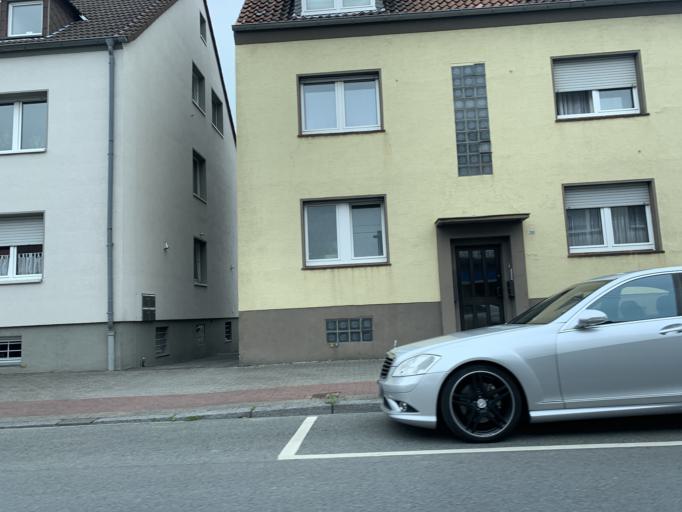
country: DE
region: North Rhine-Westphalia
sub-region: Regierungsbezirk Arnsberg
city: Hamm
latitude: 51.6642
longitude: 7.8335
